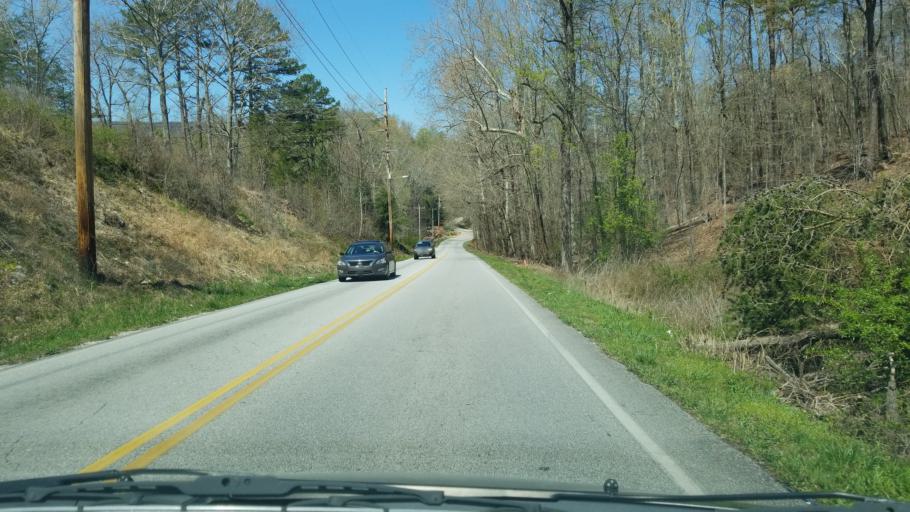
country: US
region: Tennessee
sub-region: Hamilton County
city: Middle Valley
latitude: 35.2052
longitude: -85.2122
